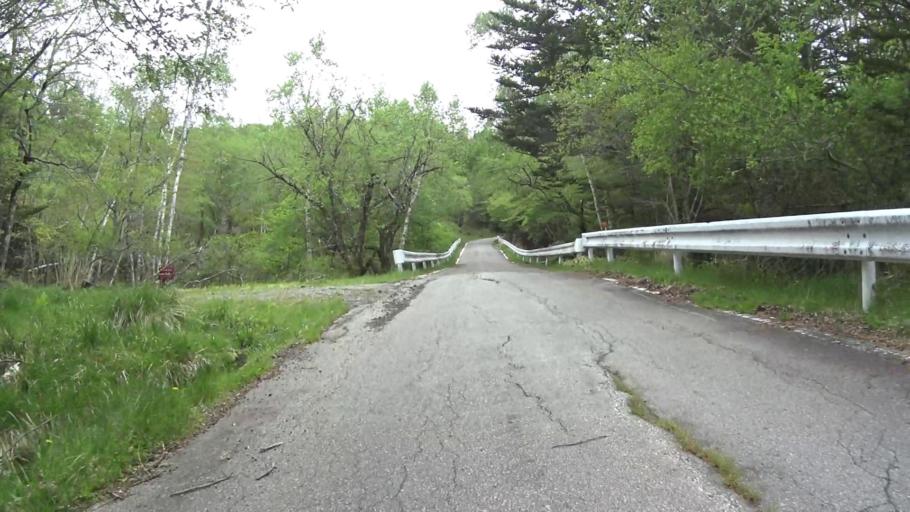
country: JP
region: Yamanashi
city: Kofu-shi
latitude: 35.8422
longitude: 138.5785
